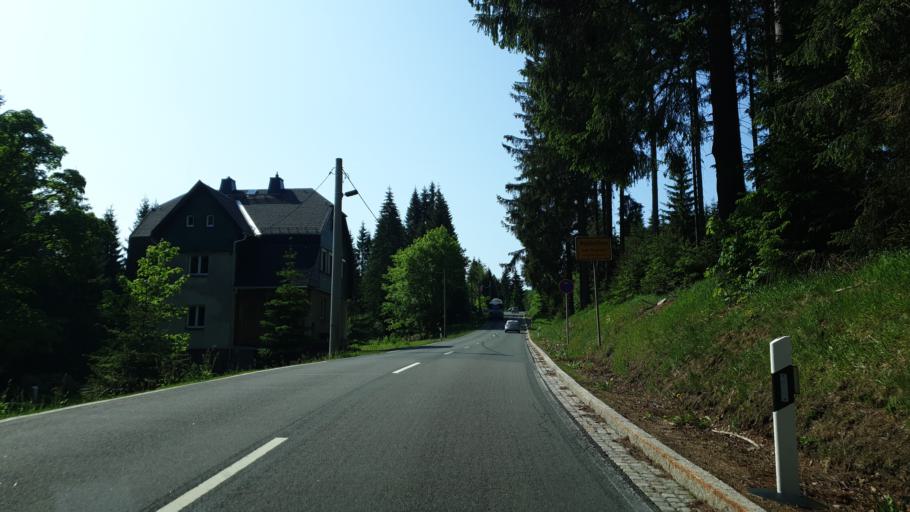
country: DE
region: Saxony
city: Tannenbergsthal
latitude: 50.4127
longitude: 12.4848
